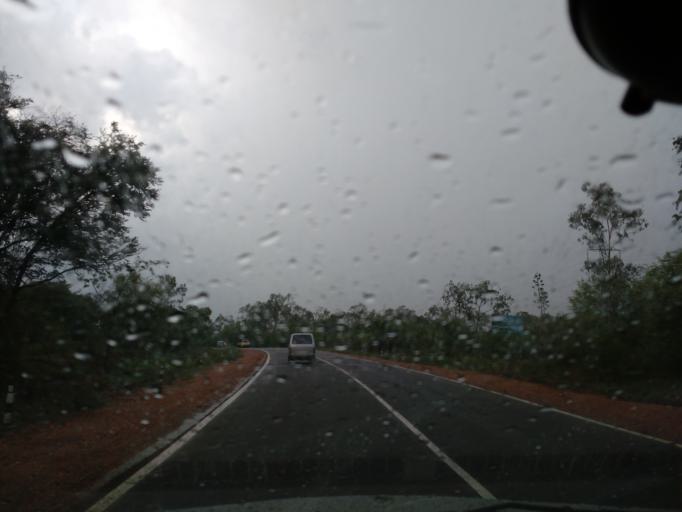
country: IN
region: Karnataka
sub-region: Tumkur
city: Tiptur
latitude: 13.2972
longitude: 76.5891
